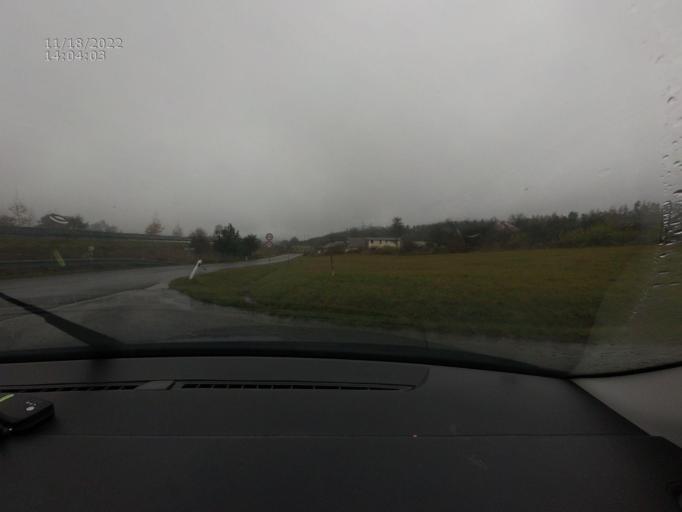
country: CZ
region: Jihocesky
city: Mirotice
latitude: 49.3545
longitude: 14.0554
